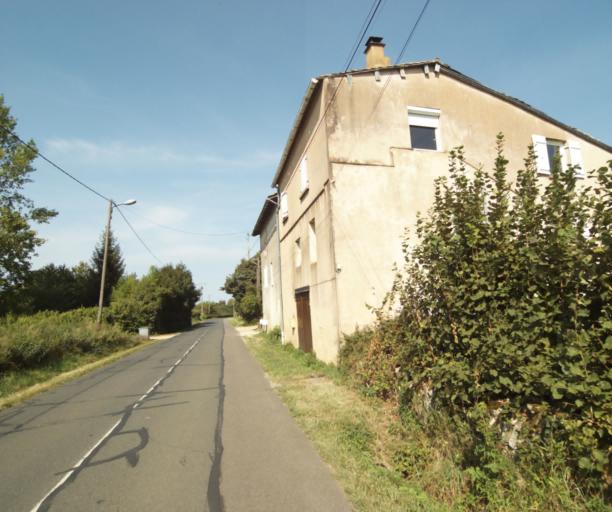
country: FR
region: Bourgogne
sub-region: Departement de Saone-et-Loire
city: Tournus
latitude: 46.5441
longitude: 4.8933
